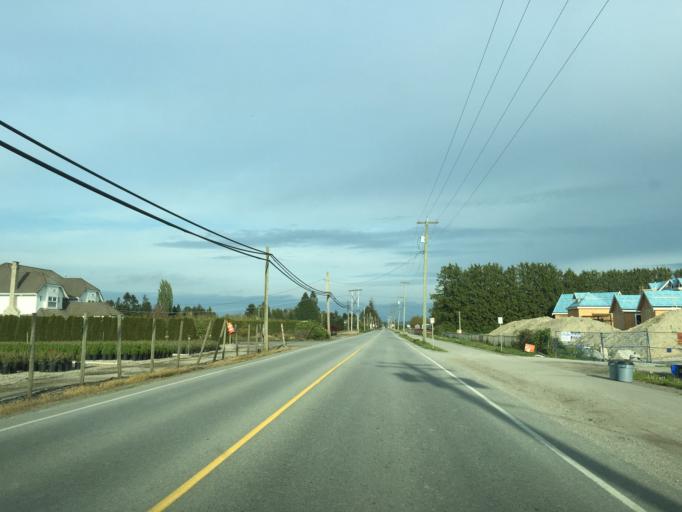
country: CA
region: British Columbia
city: Ladner
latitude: 49.1699
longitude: -123.0402
